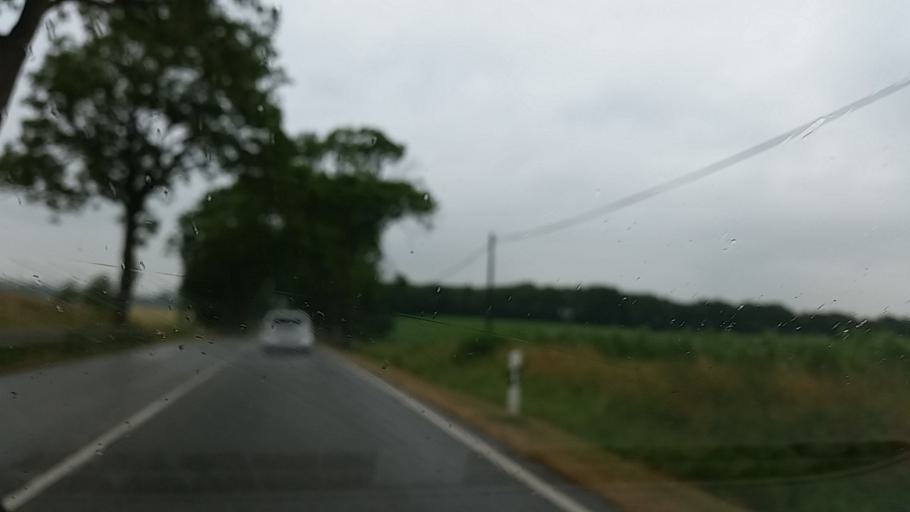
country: DE
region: Mecklenburg-Vorpommern
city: Kropelin
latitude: 54.0642
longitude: 11.7709
